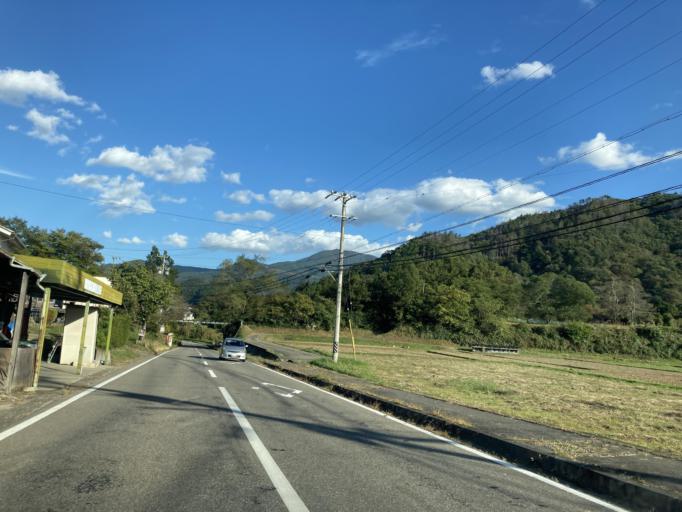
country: JP
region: Nagano
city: Omachi
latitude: 36.4395
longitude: 137.9964
